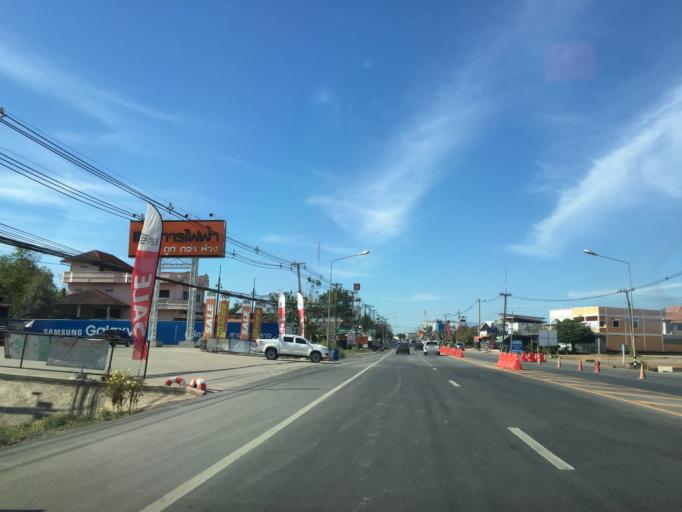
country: TH
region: Changwat Nong Bua Lamphu
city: Na Klang
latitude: 17.2986
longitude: 102.2087
